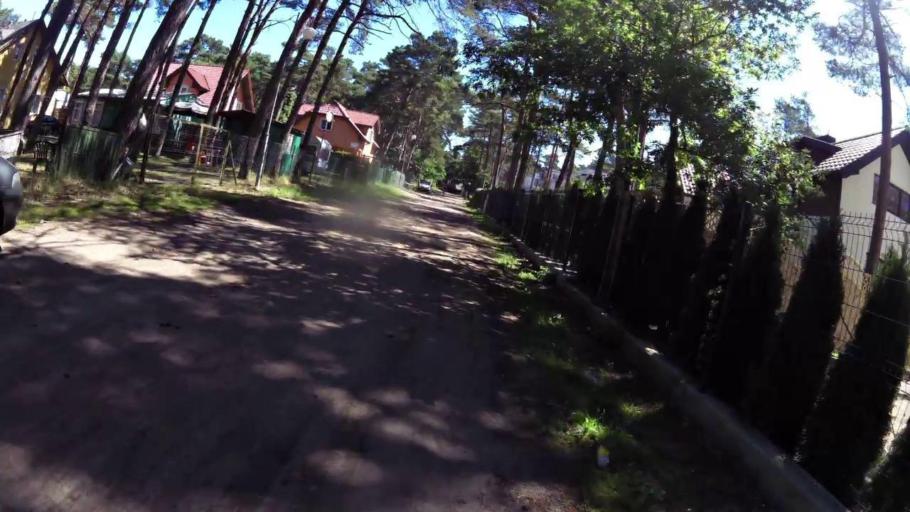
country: PL
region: West Pomeranian Voivodeship
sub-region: Powiat gryficki
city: Pobierowo
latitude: 54.0568
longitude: 14.9190
